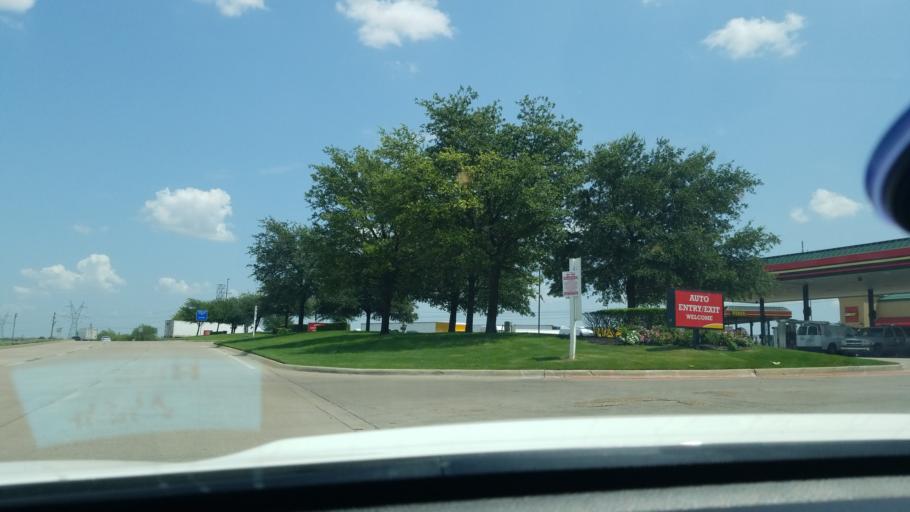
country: US
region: Texas
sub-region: Tarrant County
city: Haslet
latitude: 32.9585
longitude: -97.3081
